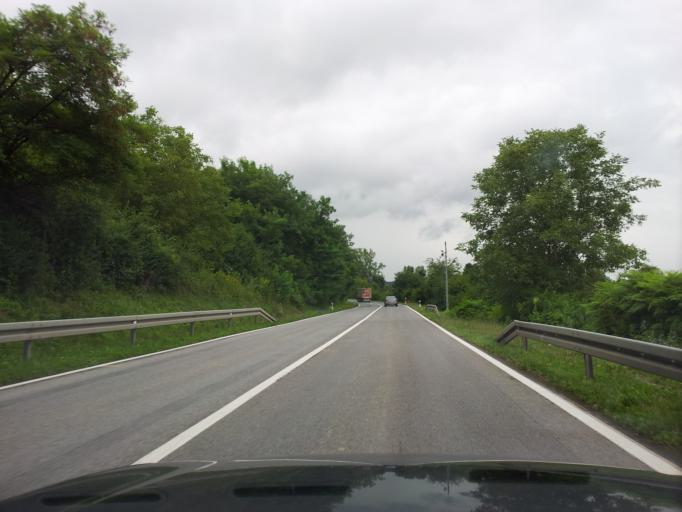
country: HR
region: Karlovacka
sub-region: Grad Karlovac
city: Karlovac
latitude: 45.4168
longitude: 15.6070
